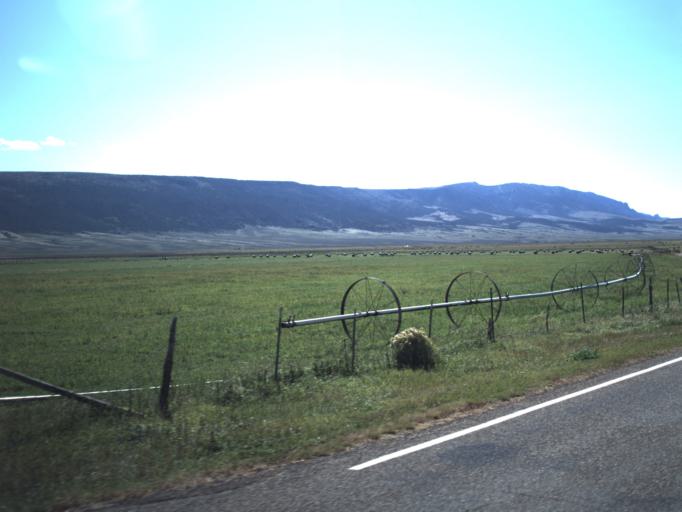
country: US
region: Utah
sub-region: Sevier County
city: Monroe
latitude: 38.4627
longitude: -111.9088
